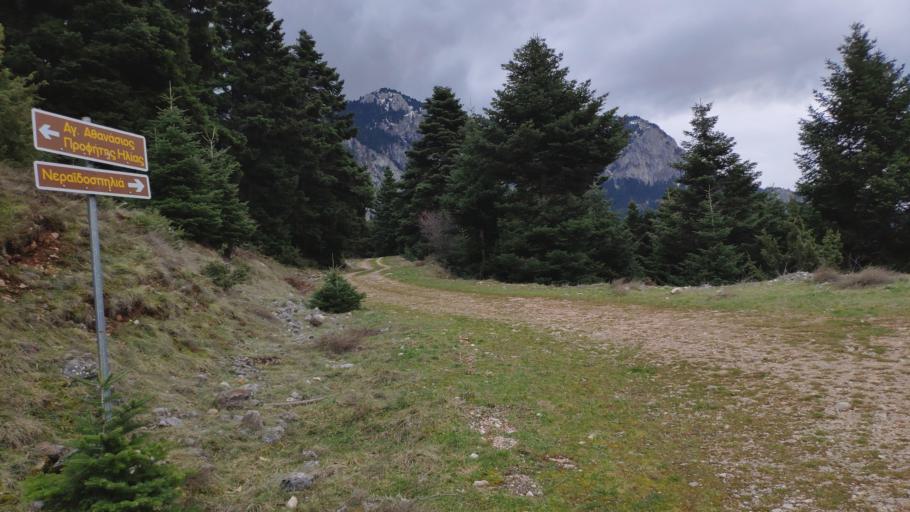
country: GR
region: Central Greece
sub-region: Nomos Fokidos
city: Amfissa
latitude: 38.6382
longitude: 22.4258
